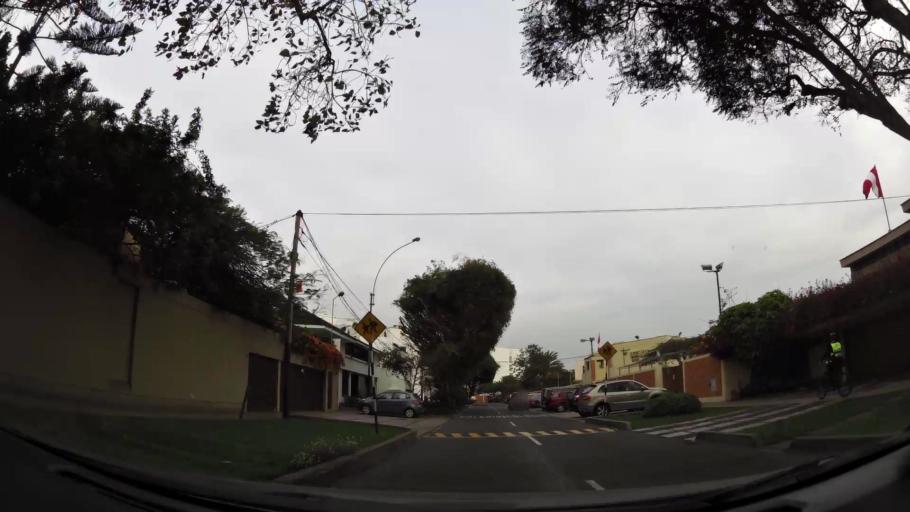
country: PE
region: Lima
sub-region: Lima
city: San Isidro
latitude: -12.1031
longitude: -77.0466
